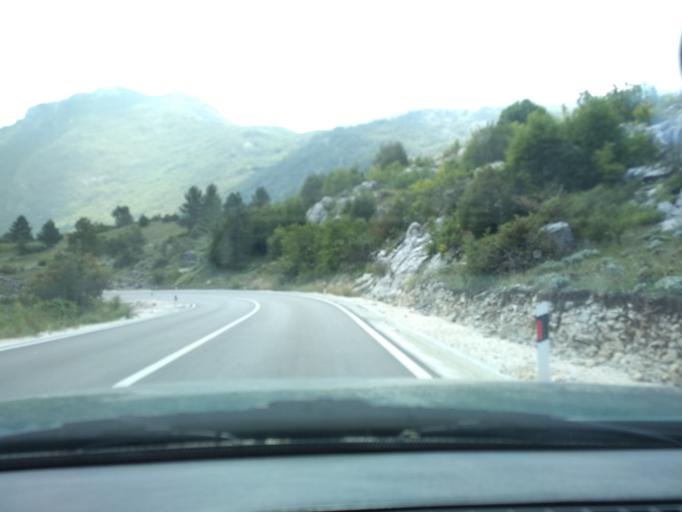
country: ME
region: Kotor
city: Kotor
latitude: 42.4301
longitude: 18.8138
